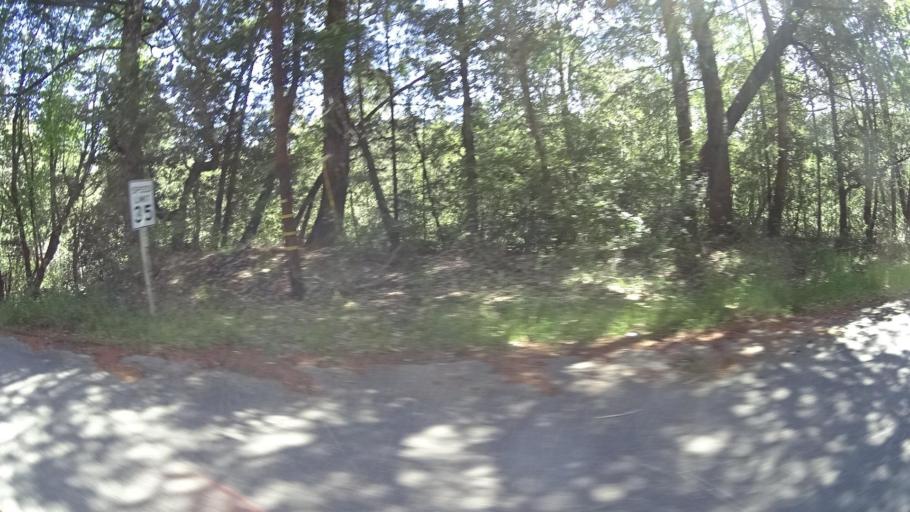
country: US
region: California
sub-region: Humboldt County
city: Rio Dell
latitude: 40.2323
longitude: -124.1541
